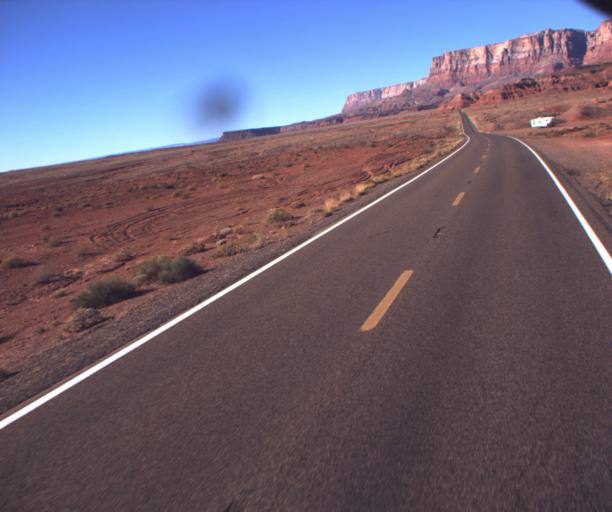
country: US
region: Arizona
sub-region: Coconino County
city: Page
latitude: 36.8127
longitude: -111.6547
